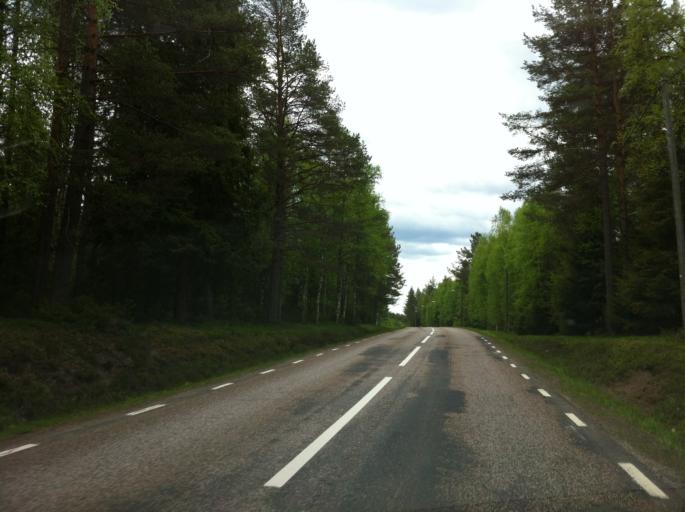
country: SE
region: Dalarna
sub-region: Malung-Saelens kommun
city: Malung
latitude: 61.2395
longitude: 13.2139
